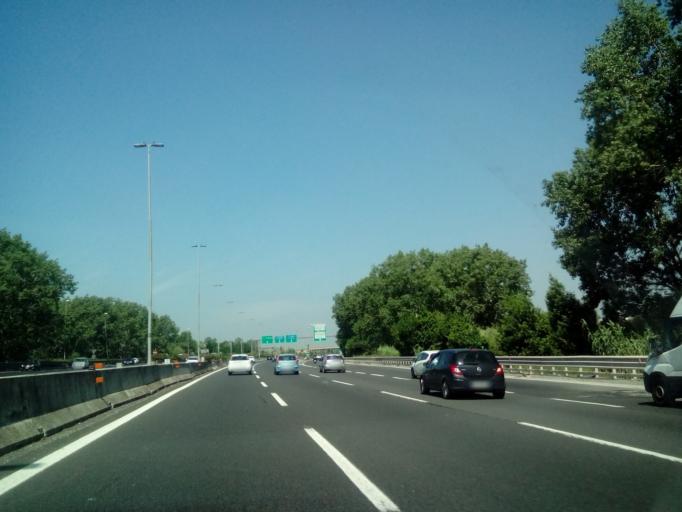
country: IT
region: Latium
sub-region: Citta metropolitana di Roma Capitale
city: Vitinia
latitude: 41.8106
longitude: 12.4025
